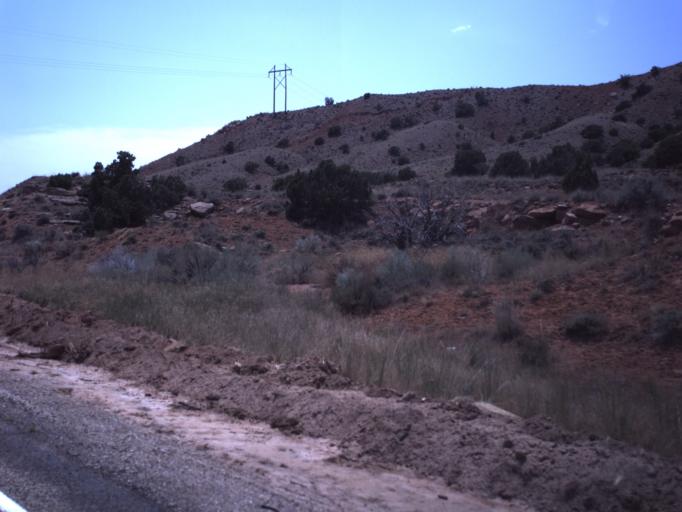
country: US
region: Utah
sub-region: Uintah County
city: Maeser
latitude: 40.4244
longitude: -109.6677
